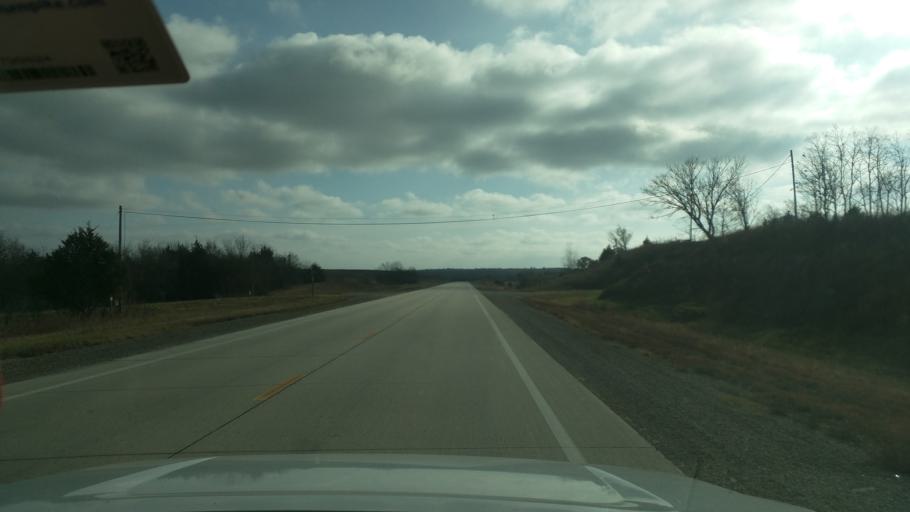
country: US
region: Kansas
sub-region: Chautauqua County
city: Sedan
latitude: 37.0731
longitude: -96.0741
